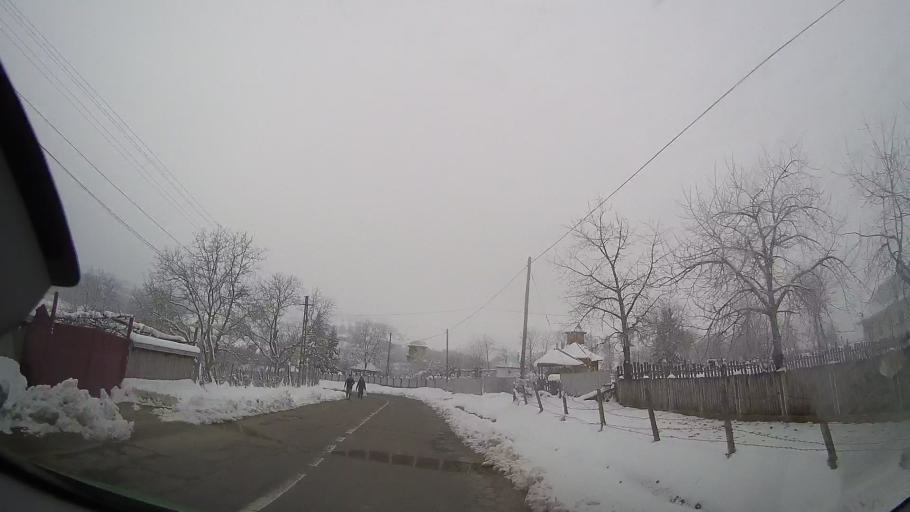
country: RO
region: Neamt
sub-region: Comuna Bozieni
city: Bozieni
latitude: 46.8356
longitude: 27.1641
